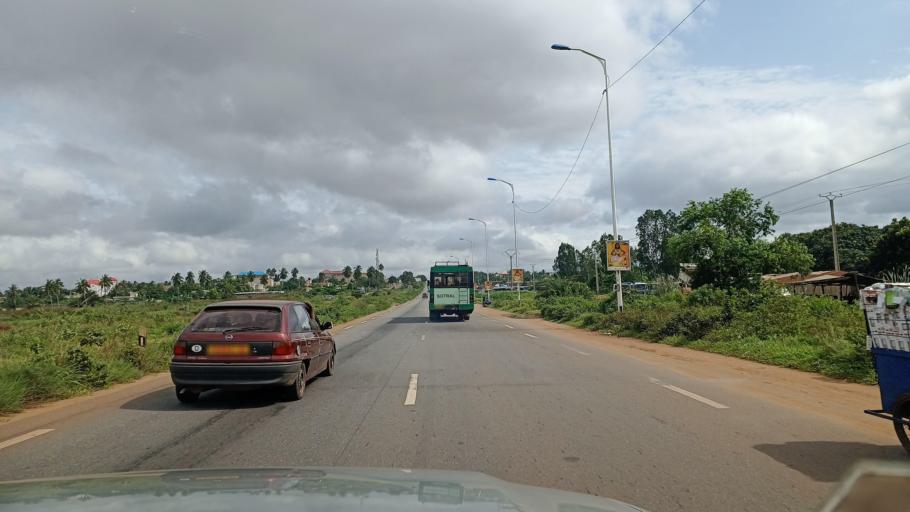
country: TG
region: Maritime
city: Tsevie
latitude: 6.3128
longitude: 1.2174
